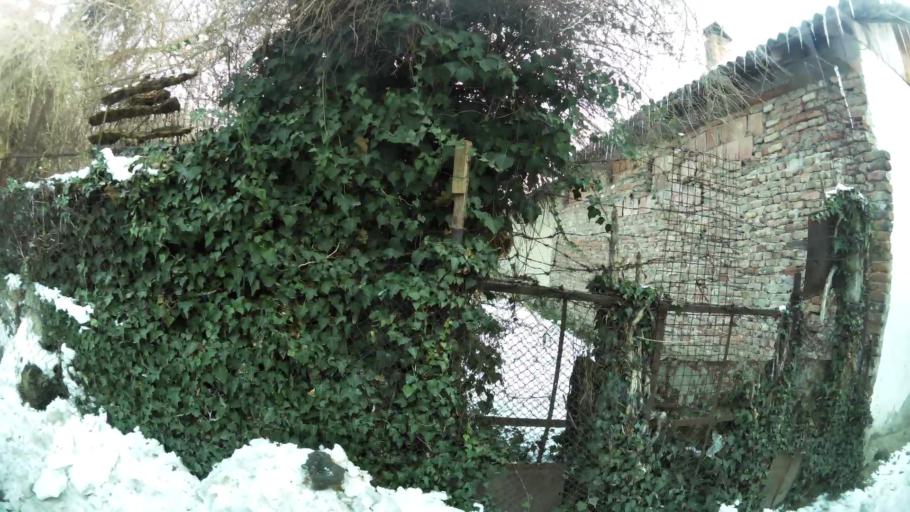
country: MK
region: Cair
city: Cair
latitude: 42.0122
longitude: 21.4384
